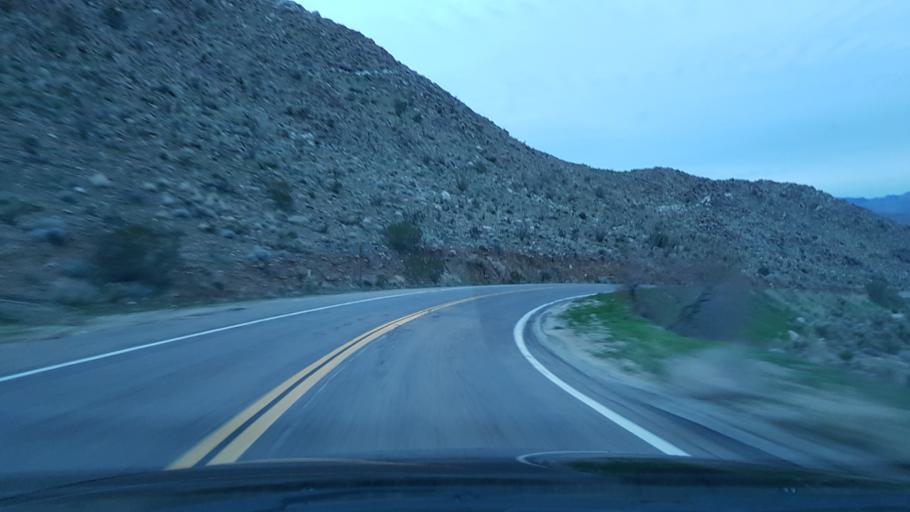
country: US
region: California
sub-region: San Diego County
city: Julian
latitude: 33.0400
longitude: -116.4112
